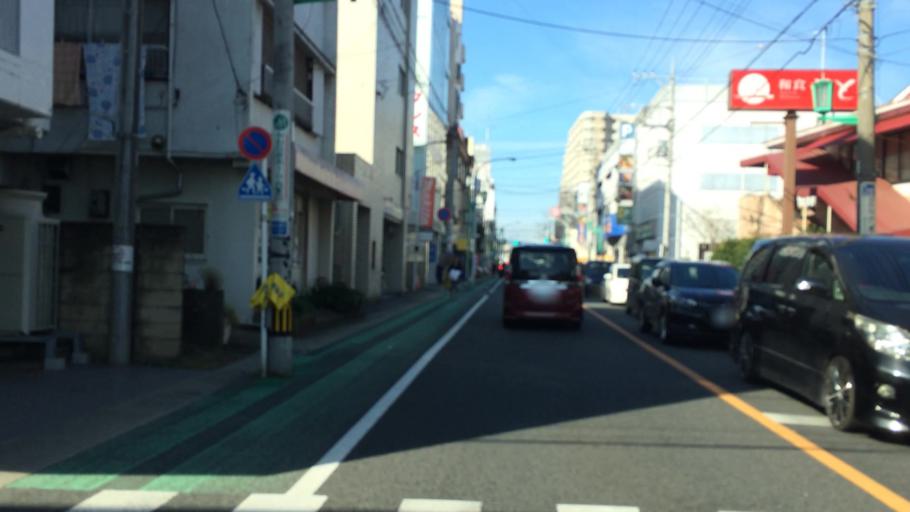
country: JP
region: Tokyo
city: Hino
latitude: 35.7012
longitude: 139.3963
